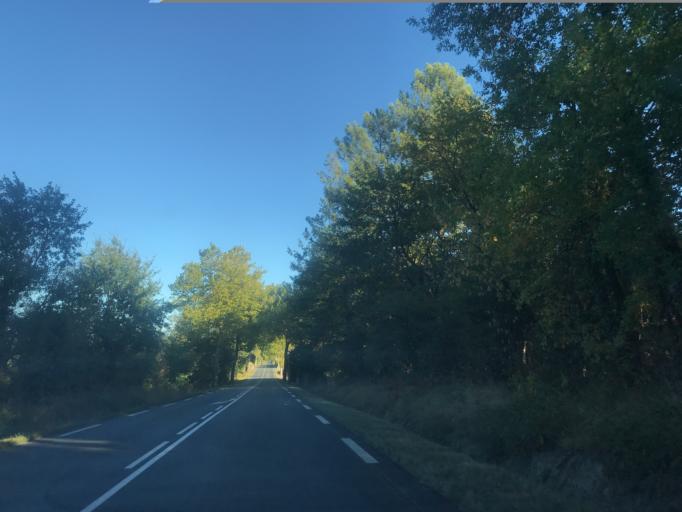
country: FR
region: Poitou-Charentes
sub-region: Departement de la Charente-Maritime
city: Saint-Aigulin
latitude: 45.1740
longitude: -0.0722
